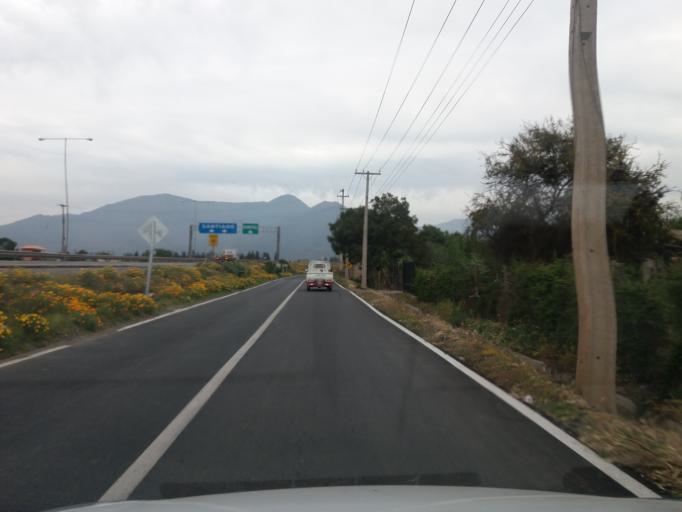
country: CL
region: Valparaiso
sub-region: Provincia de Quillota
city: Hacienda La Calera
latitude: -32.8402
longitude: -71.1123
